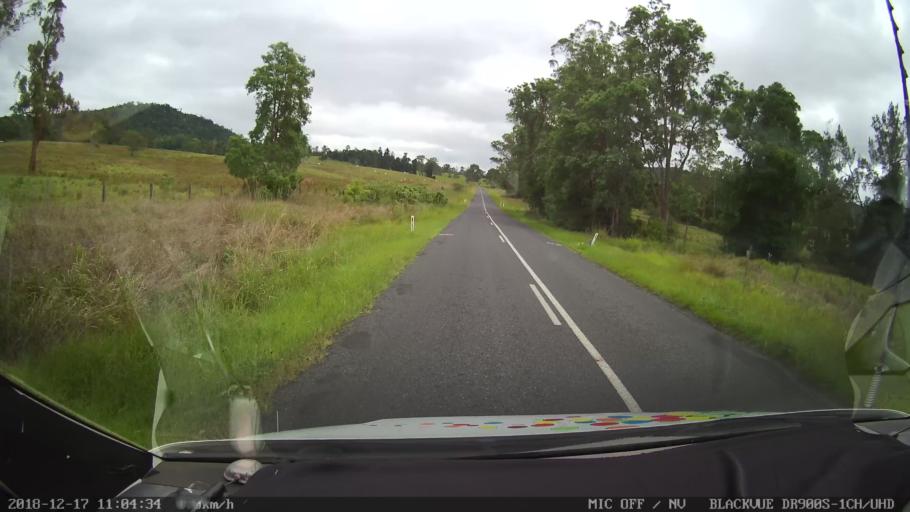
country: AU
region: New South Wales
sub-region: Kyogle
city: Kyogle
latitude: -28.7977
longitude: 152.6430
